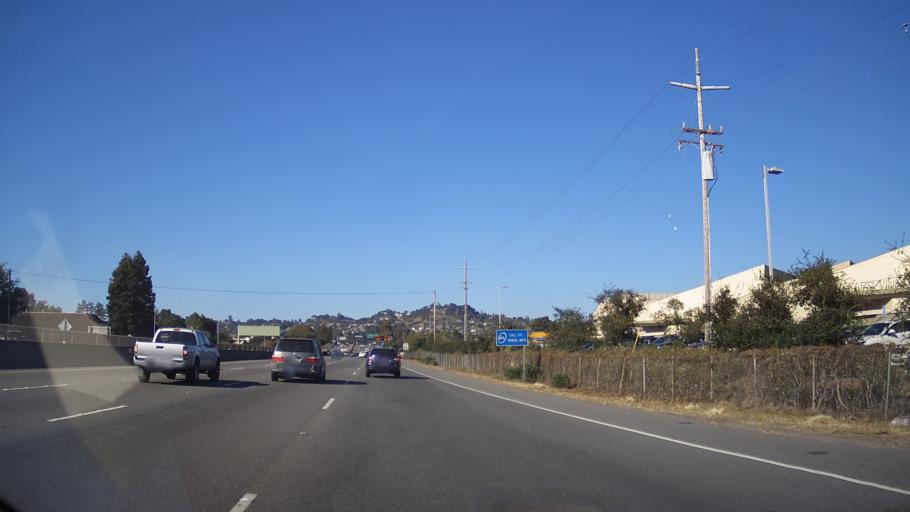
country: US
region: California
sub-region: Marin County
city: Corte Madera
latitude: 37.9297
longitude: -122.5150
